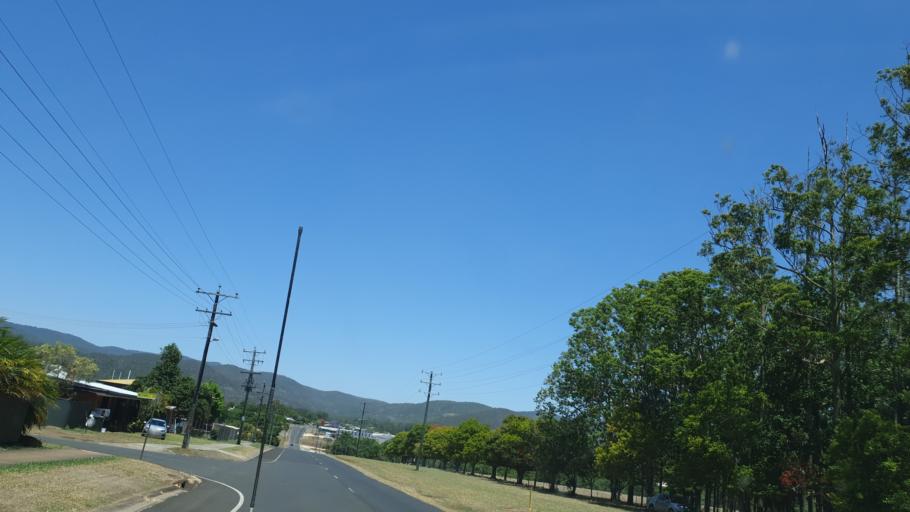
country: AU
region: Queensland
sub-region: Tablelands
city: Atherton
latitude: -17.2575
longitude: 145.4834
